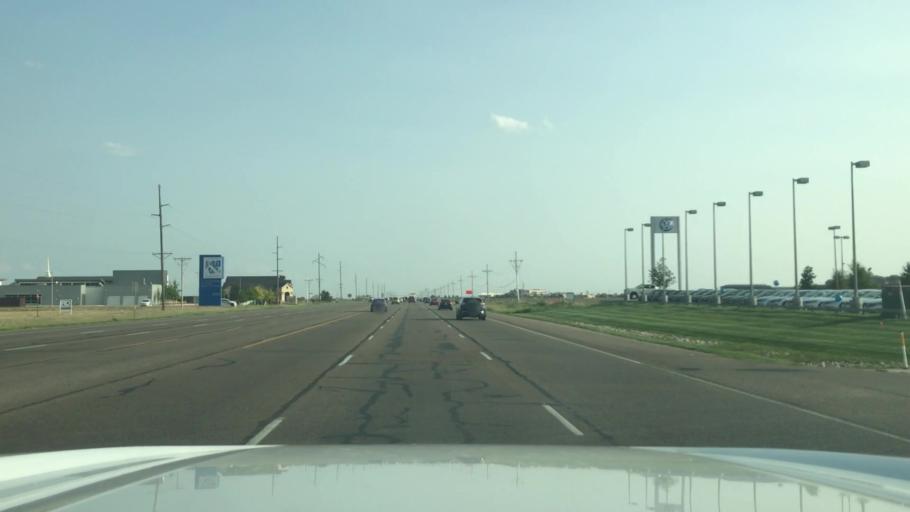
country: US
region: Texas
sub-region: Potter County
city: Amarillo
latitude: 35.1582
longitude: -101.9383
